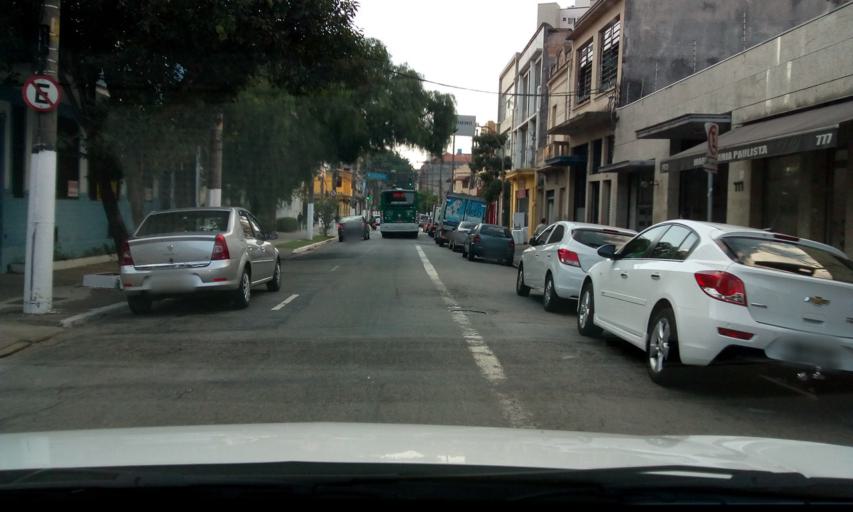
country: BR
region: Sao Paulo
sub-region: Sao Paulo
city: Sao Paulo
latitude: -23.5607
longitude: -46.6217
